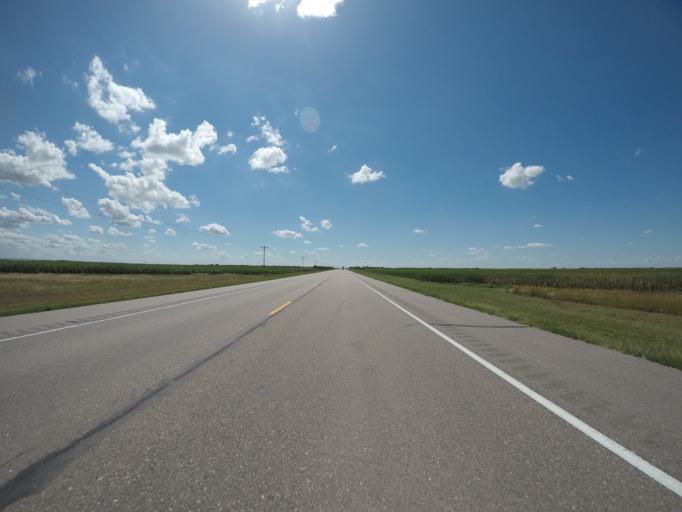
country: US
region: Nebraska
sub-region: Chase County
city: Imperial
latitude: 40.4950
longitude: -101.5545
